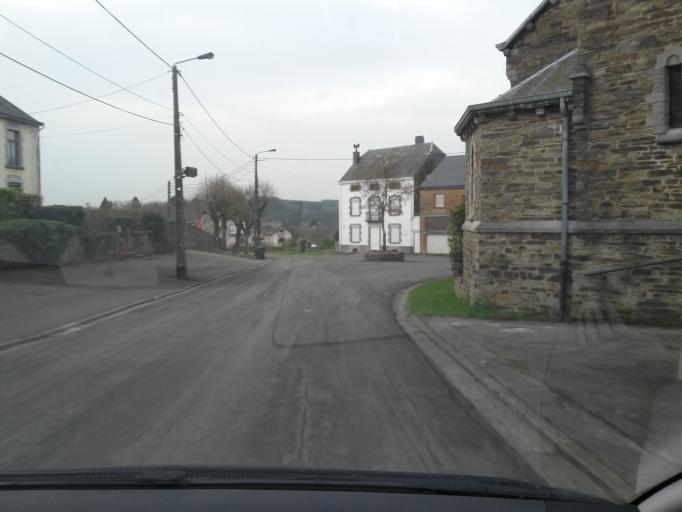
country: BE
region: Wallonia
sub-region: Province du Luxembourg
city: Herbeumont
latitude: 49.7817
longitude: 5.2349
